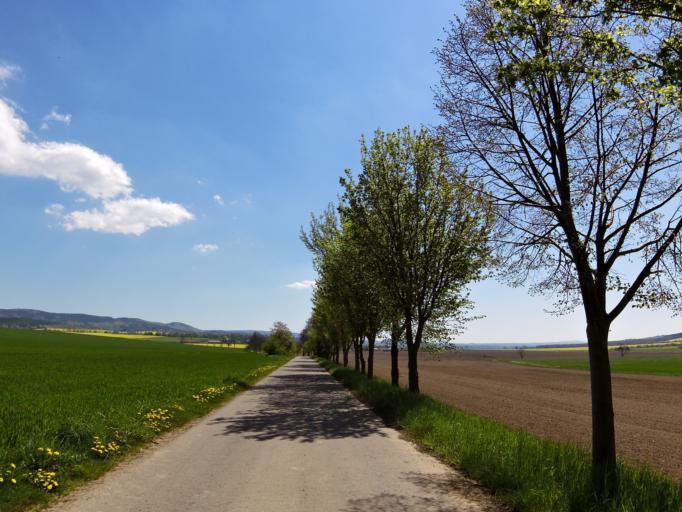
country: DE
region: Thuringia
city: Bad Salzungen
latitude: 50.8678
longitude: 10.2322
